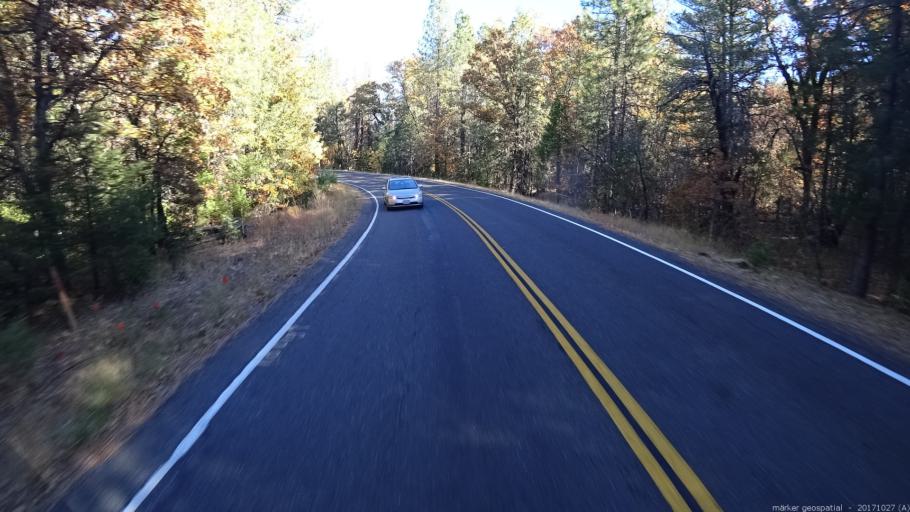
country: US
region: California
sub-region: Shasta County
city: Burney
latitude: 40.9132
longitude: -121.9080
